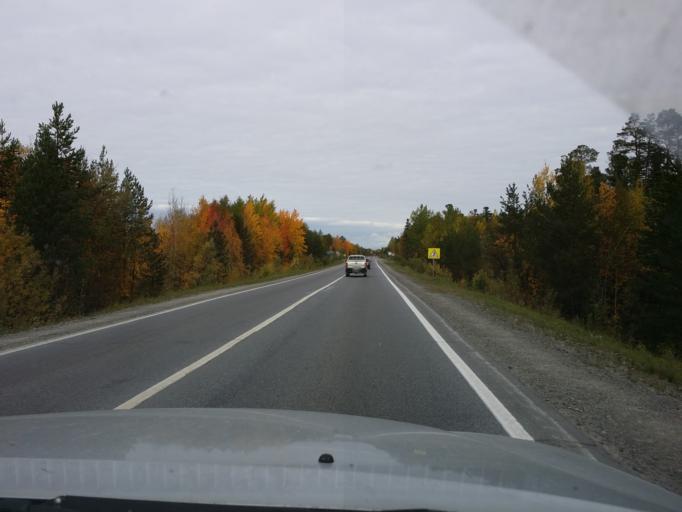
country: RU
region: Khanty-Mansiyskiy Avtonomnyy Okrug
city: Megion
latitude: 61.1038
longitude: 75.8537
